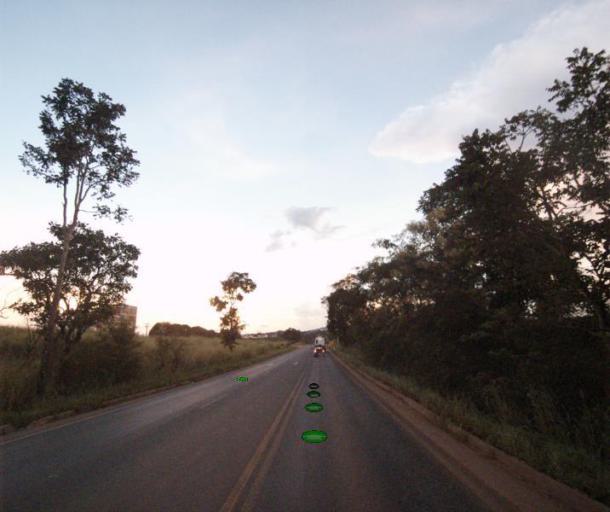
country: BR
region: Goias
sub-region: Uruacu
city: Uruacu
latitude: -14.4963
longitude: -49.1513
